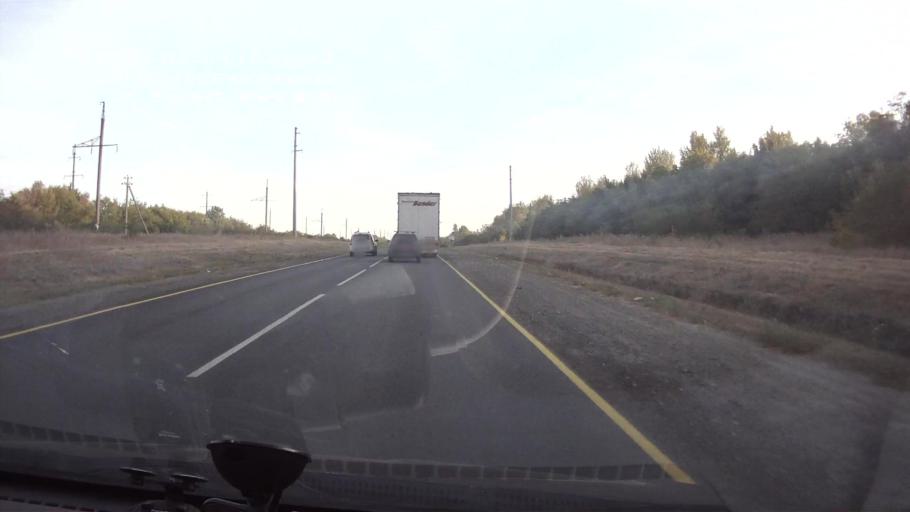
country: RU
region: Saratov
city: Krasnoarmeysk
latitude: 51.1636
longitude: 45.6491
